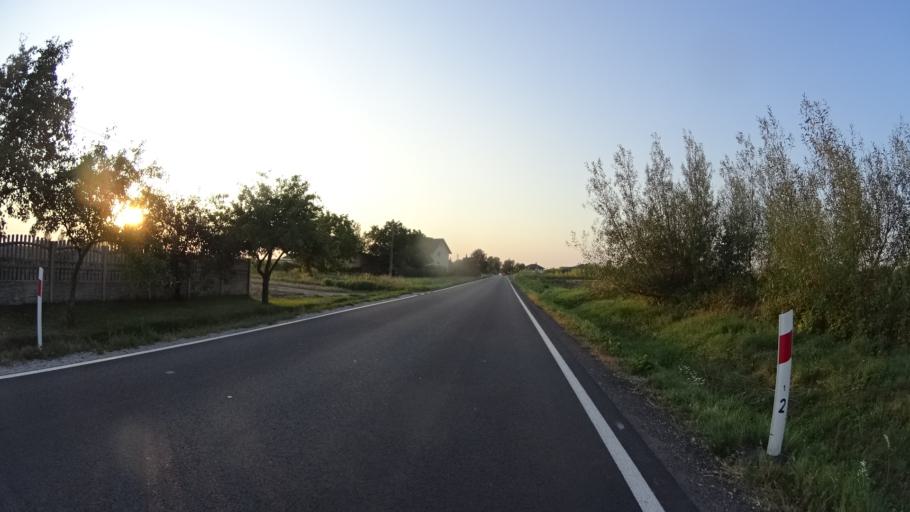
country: PL
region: Masovian Voivodeship
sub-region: Powiat warszawski zachodni
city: Ozarow Mazowiecki
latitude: 52.2435
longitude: 20.7483
